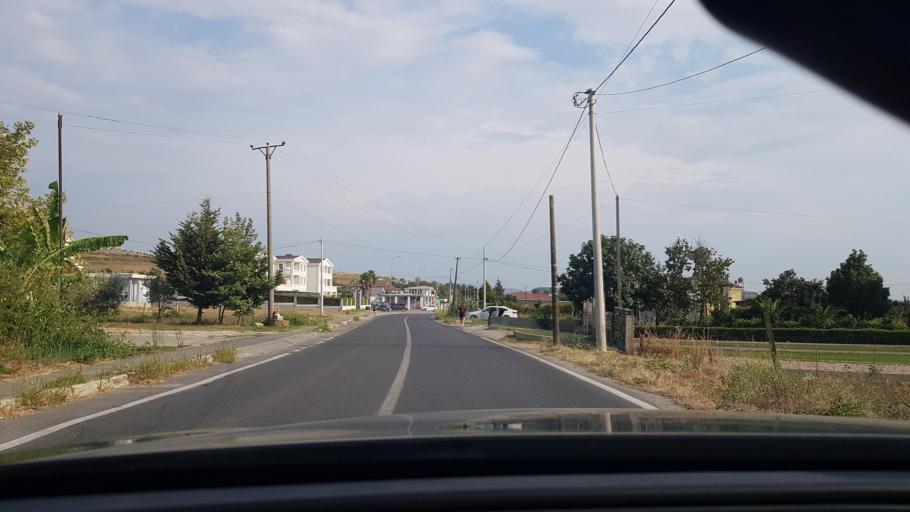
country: AL
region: Durres
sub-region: Rrethi i Durresit
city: Manze
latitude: 41.4643
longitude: 19.5627
